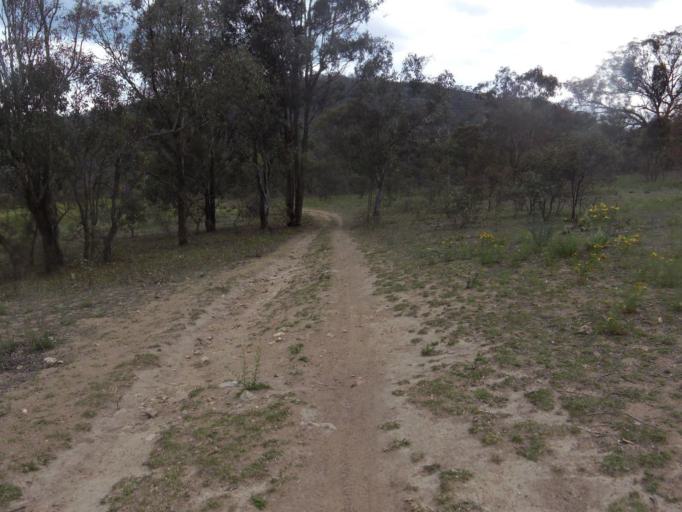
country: AU
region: Australian Capital Territory
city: Forrest
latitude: -35.3538
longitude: 149.1172
